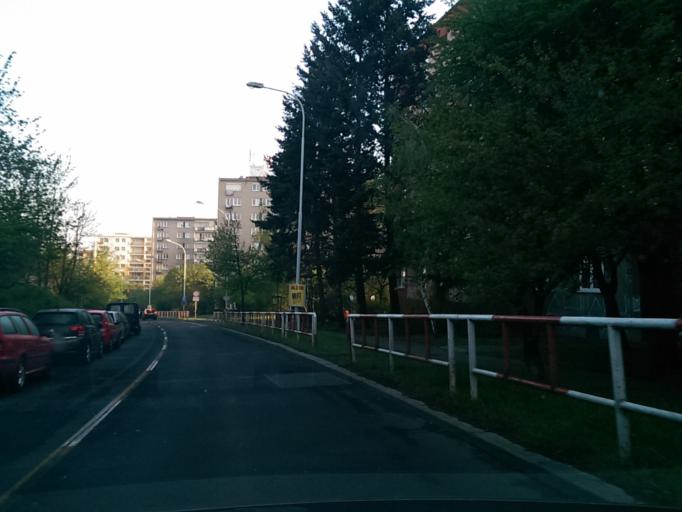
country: CZ
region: Praha
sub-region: Praha 8
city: Karlin
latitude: 50.0441
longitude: 14.4898
